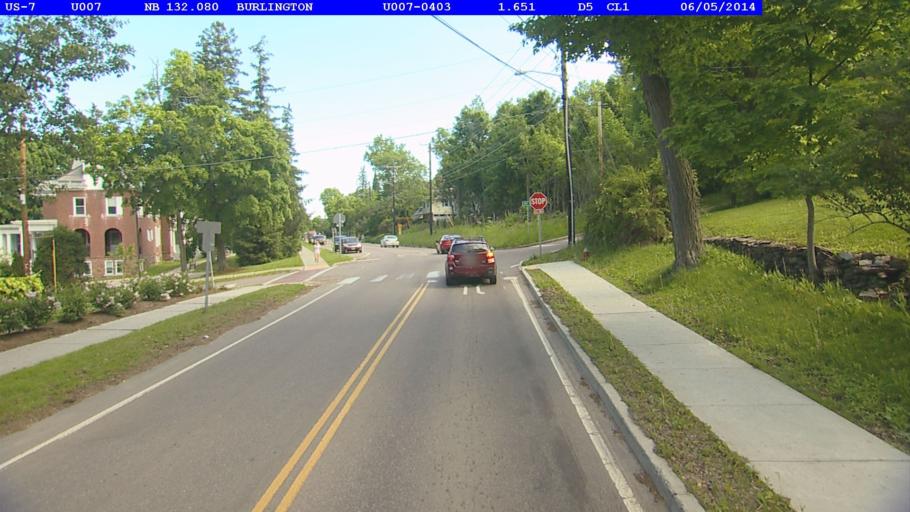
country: US
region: Vermont
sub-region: Chittenden County
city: Burlington
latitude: 44.4693
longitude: -73.2051
